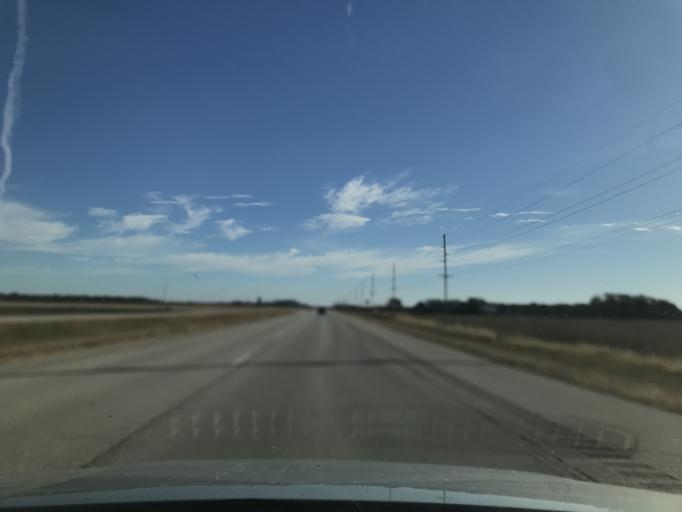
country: US
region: Illinois
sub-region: Hancock County
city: Carthage
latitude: 40.4151
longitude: -91.0571
